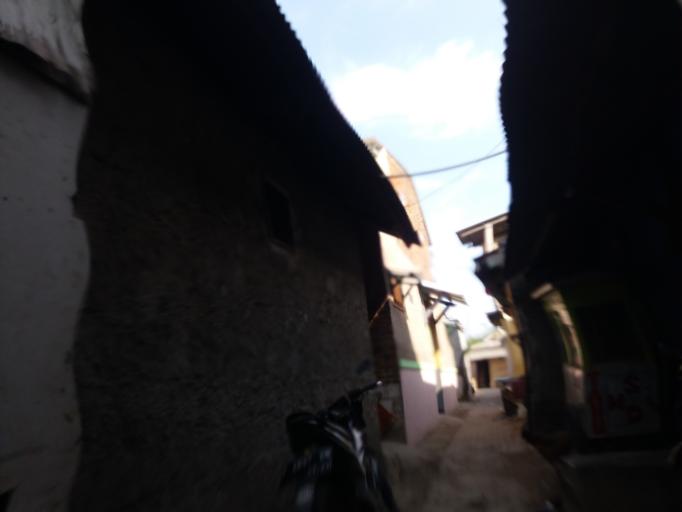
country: ID
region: West Java
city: Bandung
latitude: -6.9310
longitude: 107.6648
